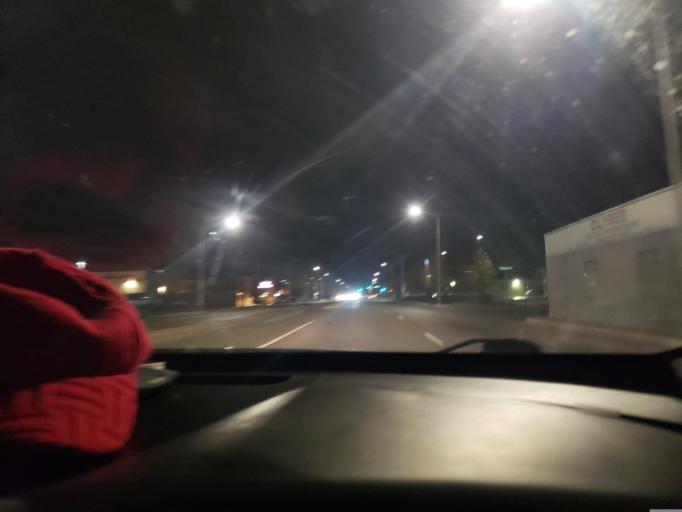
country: US
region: New Mexico
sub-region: Bernalillo County
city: Albuquerque
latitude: 35.1085
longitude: -106.6446
